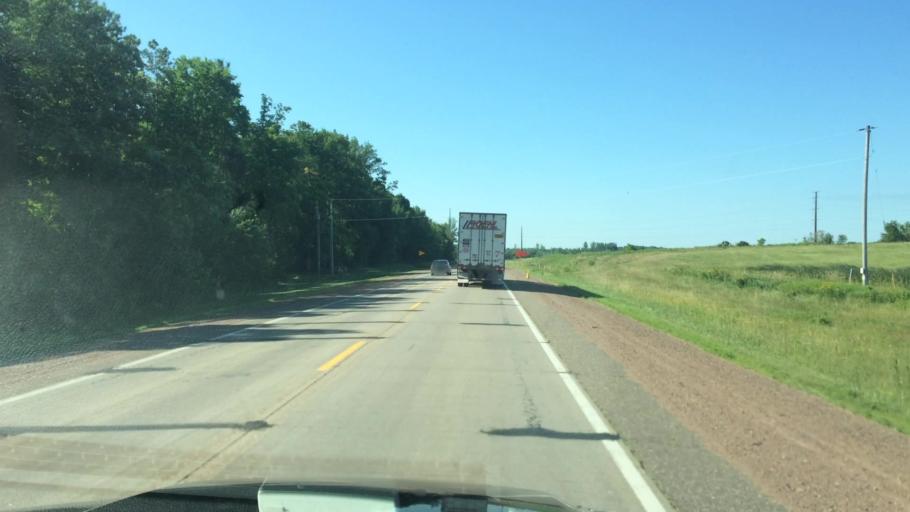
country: US
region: Wisconsin
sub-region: Marathon County
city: Athens
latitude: 44.9397
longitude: -90.0791
